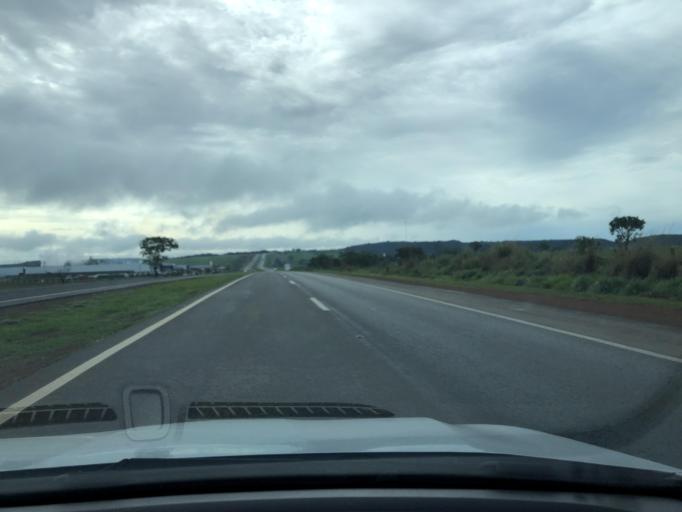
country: BR
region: Goias
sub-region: Cristalina
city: Cristalina
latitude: -16.6175
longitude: -47.7541
